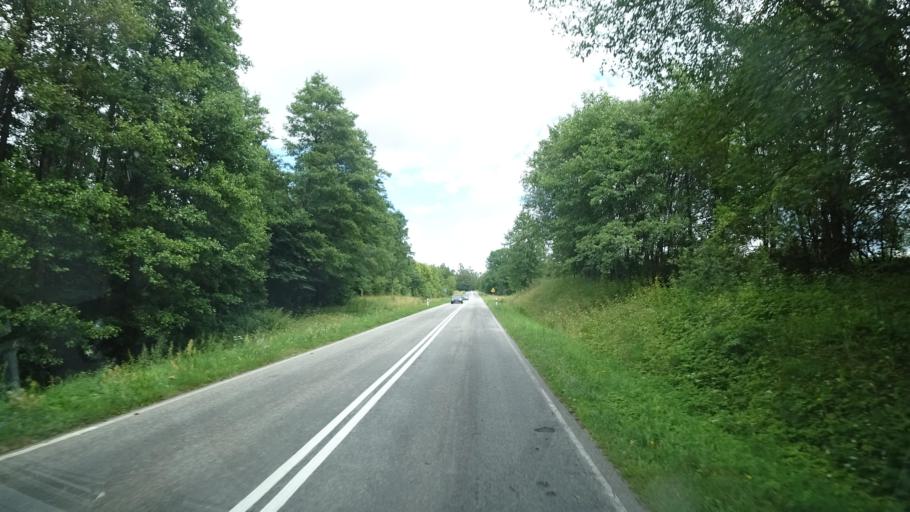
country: PL
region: Warmian-Masurian Voivodeship
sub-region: Powiat goldapski
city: Goldap
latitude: 54.2151
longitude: 22.2213
